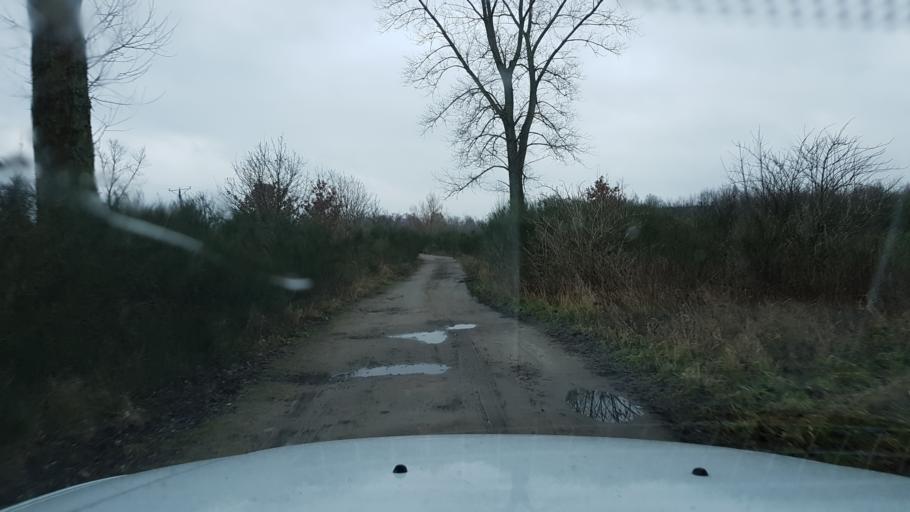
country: PL
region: West Pomeranian Voivodeship
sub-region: Powiat gryficki
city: Brojce
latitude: 53.9792
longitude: 15.3051
